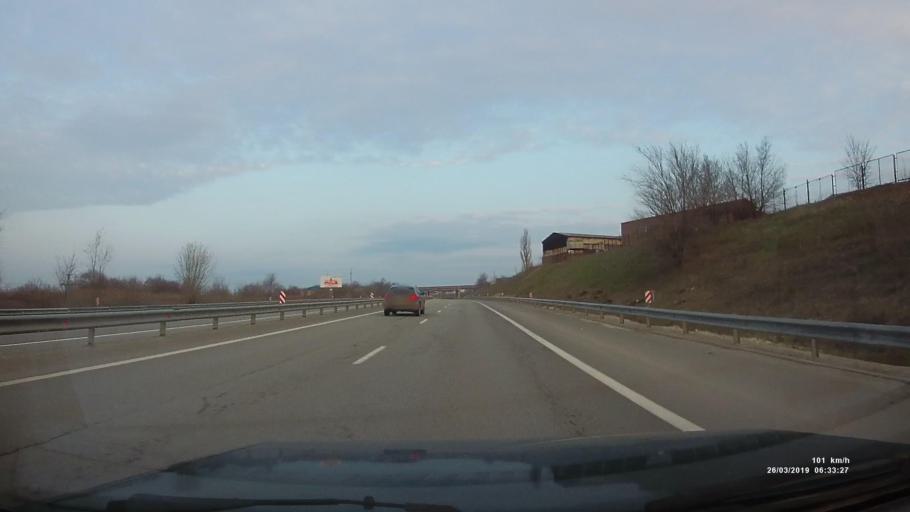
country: RU
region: Rostov
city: Chaltyr
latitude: 47.2733
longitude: 39.4881
